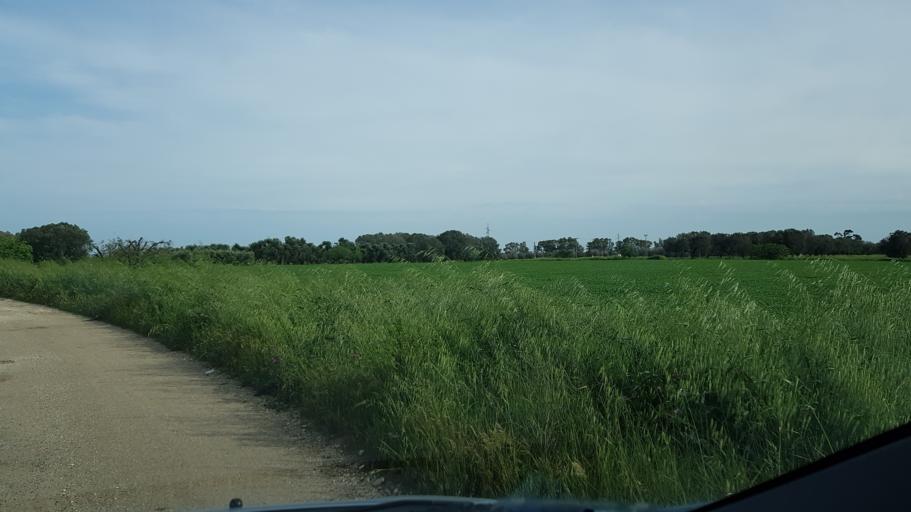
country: IT
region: Apulia
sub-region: Provincia di Brindisi
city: Tuturano
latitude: 40.5515
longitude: 17.9319
